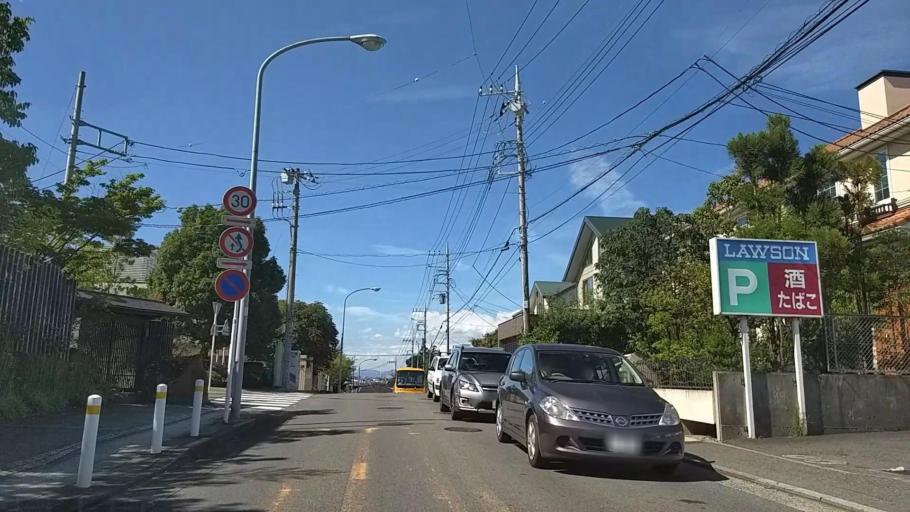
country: JP
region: Tokyo
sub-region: Machida-shi
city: Machida
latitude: 35.5606
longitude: 139.5412
